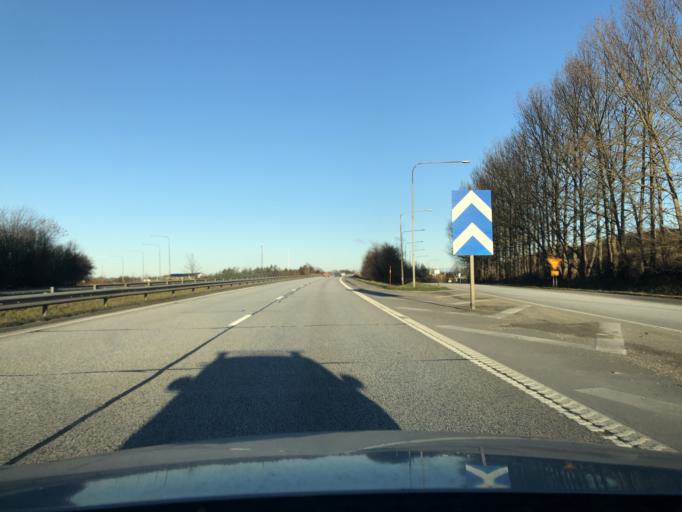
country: SE
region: Skane
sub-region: Vellinge Kommun
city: Vellinge
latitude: 55.4778
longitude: 13.0123
